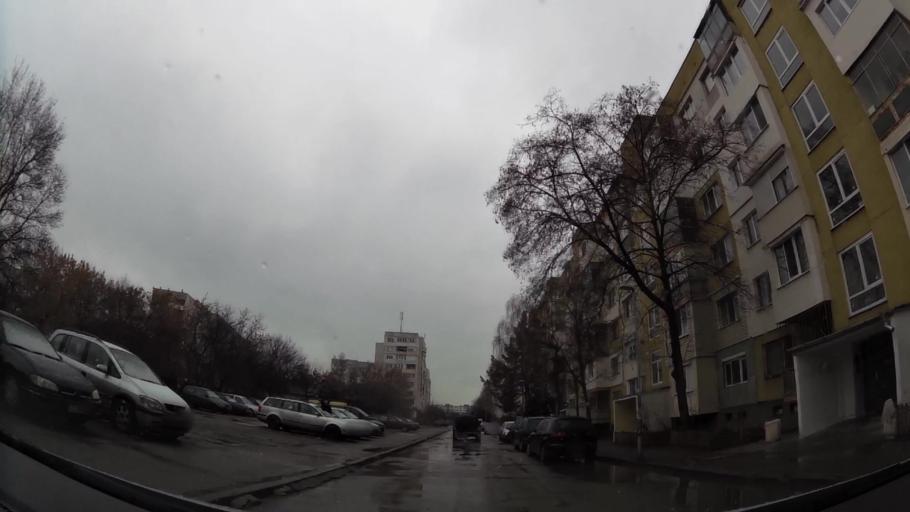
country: BG
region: Sofia-Capital
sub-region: Stolichna Obshtina
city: Sofia
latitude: 42.6679
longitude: 23.3879
